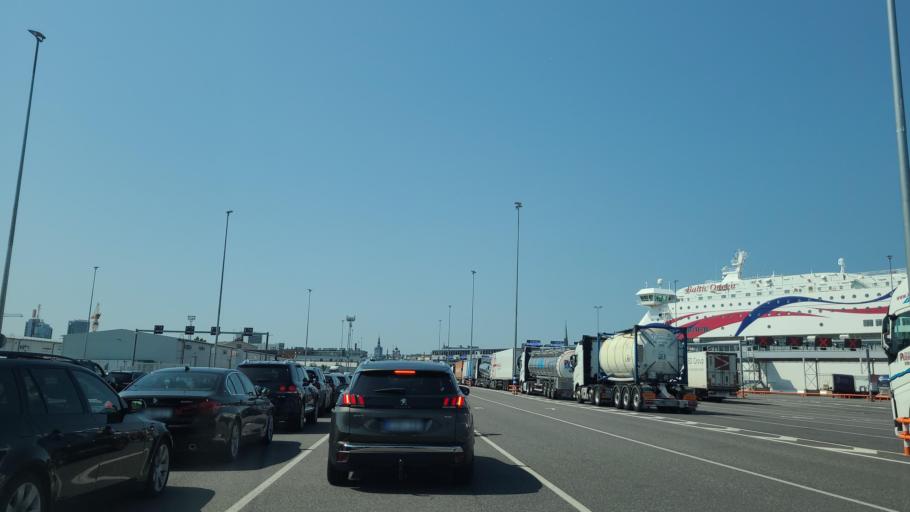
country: EE
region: Harju
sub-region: Tallinna linn
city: Tallinn
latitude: 59.4440
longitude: 24.7749
